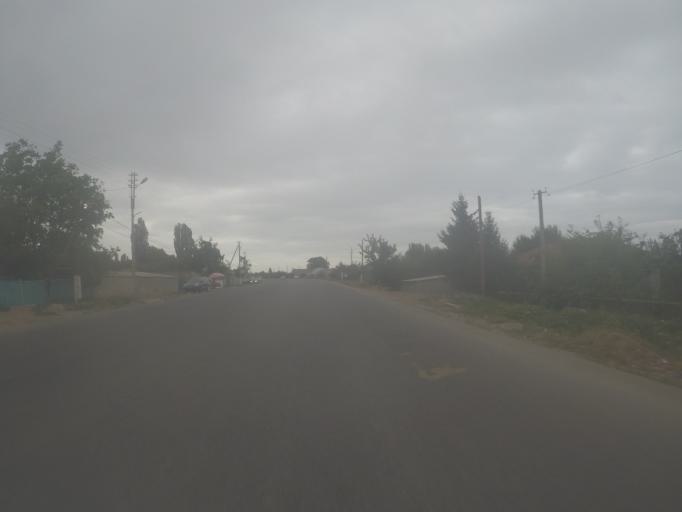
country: KG
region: Ysyk-Koel
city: Cholpon-Ata
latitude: 42.6908
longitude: 77.3616
